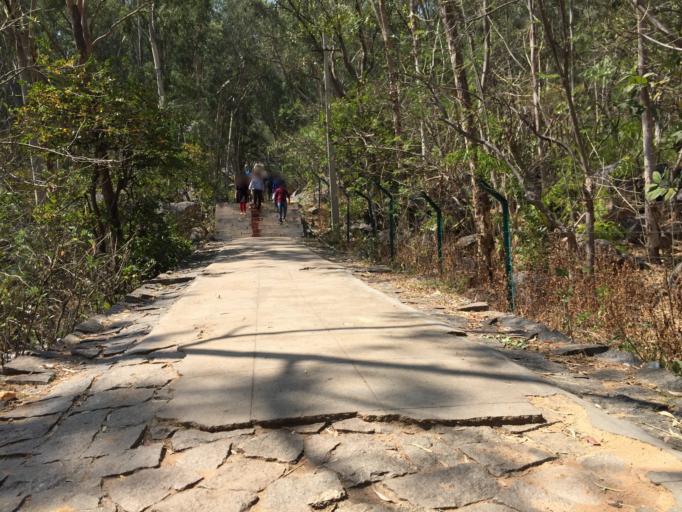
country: IN
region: Karnataka
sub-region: Kolar
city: Kolar
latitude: 13.1422
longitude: 78.1026
